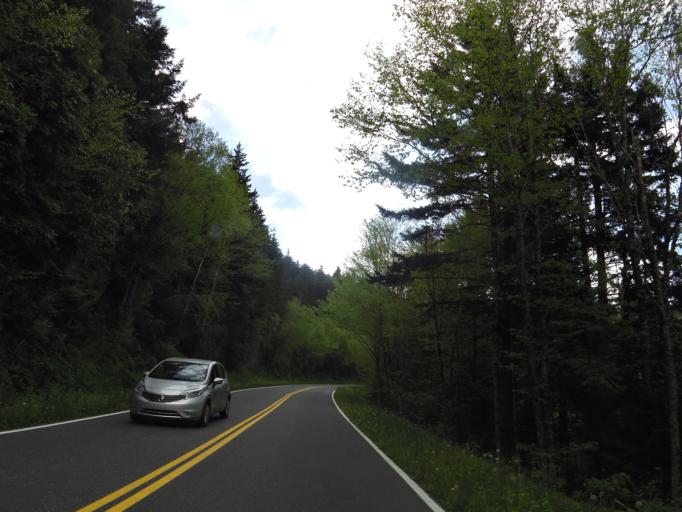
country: US
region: Tennessee
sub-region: Sevier County
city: Gatlinburg
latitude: 35.5800
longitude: -83.4779
